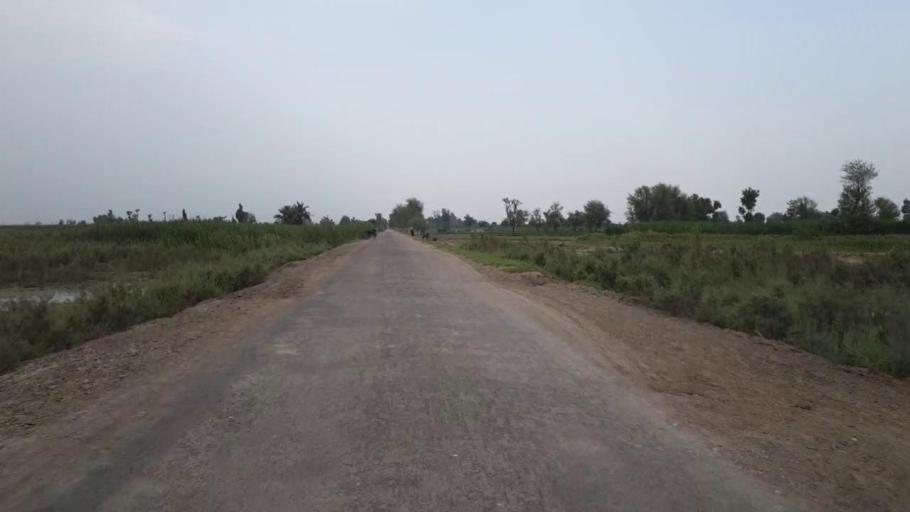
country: PK
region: Sindh
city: Bandhi
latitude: 26.5270
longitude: 68.1929
